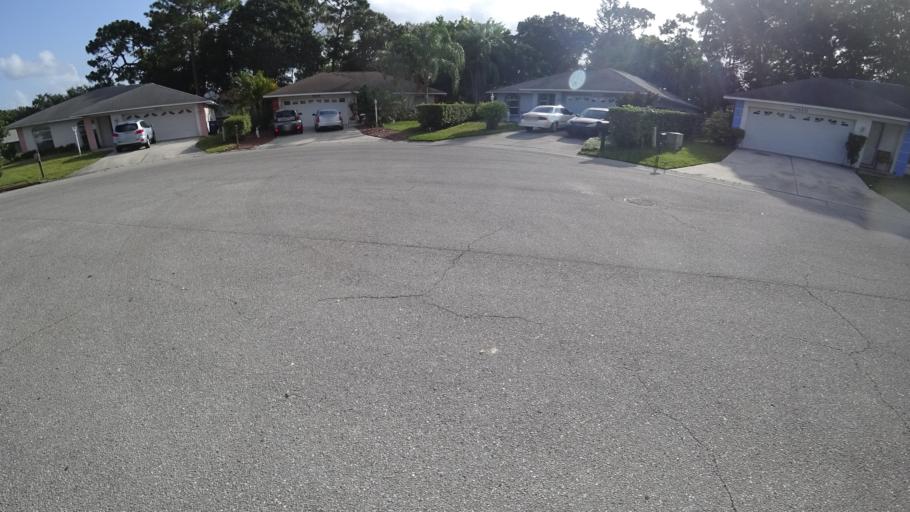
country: US
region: Florida
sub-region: Sarasota County
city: North Sarasota
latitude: 27.4051
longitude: -82.5080
